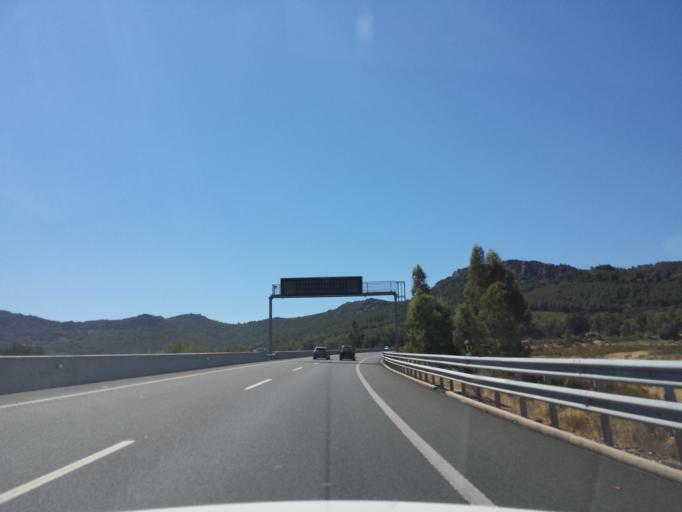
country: ES
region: Extremadura
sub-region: Provincia de Caceres
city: Higuera
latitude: 39.7069
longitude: -5.6902
